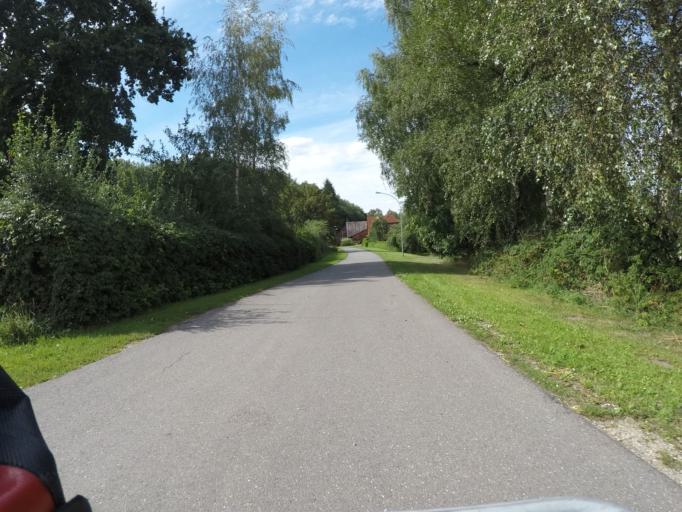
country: DE
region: Lower Saxony
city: Radbruch
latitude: 53.3619
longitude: 10.3006
